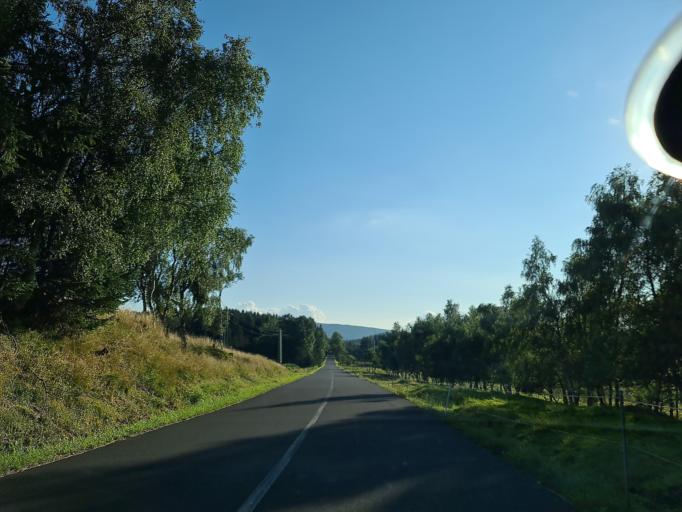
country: DE
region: Saxony
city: Deutschneudorf
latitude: 50.6211
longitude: 13.4882
